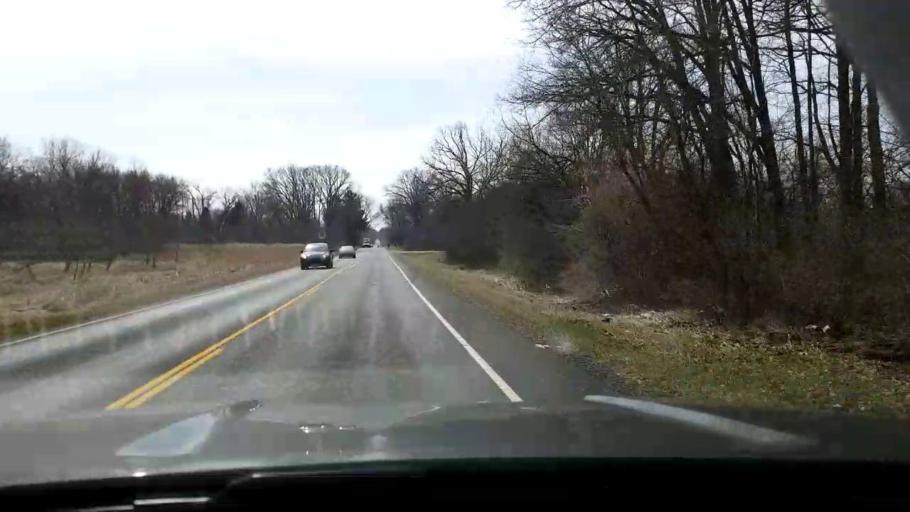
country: US
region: Michigan
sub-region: Jackson County
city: Spring Arbor
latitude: 42.2014
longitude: -84.5210
